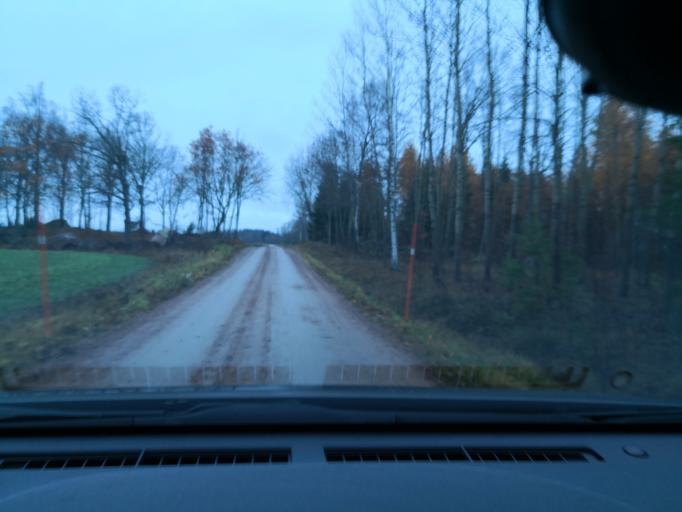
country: SE
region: Vaestmanland
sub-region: Hallstahammars Kommun
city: Kolback
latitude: 59.5553
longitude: 16.1878
